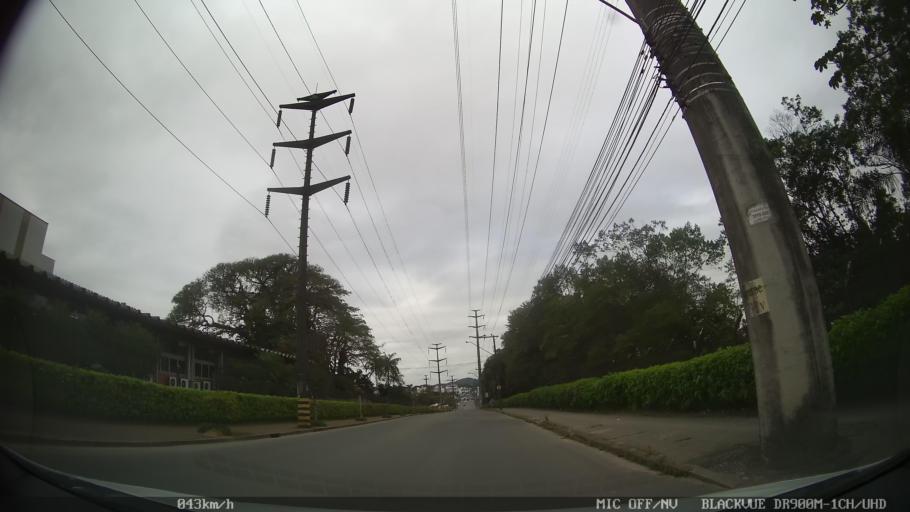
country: BR
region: Santa Catarina
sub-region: Joinville
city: Joinville
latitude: -26.2626
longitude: -48.8725
